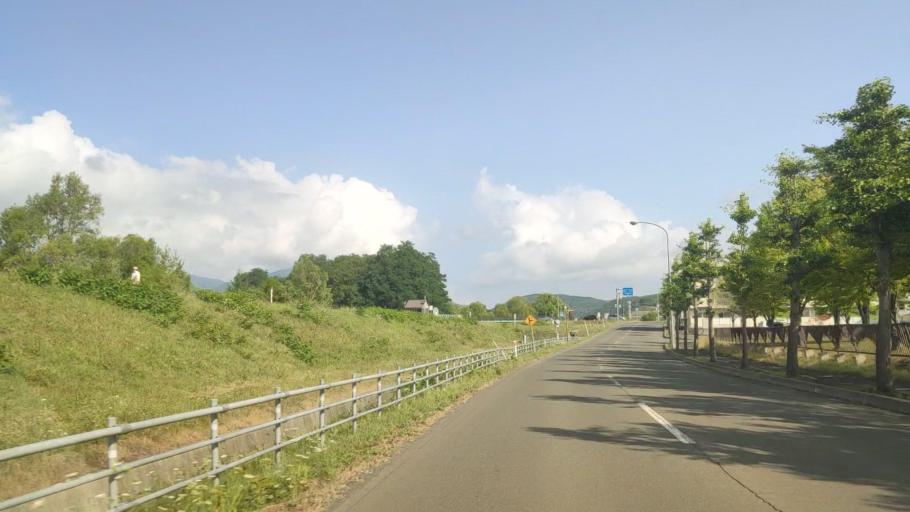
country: JP
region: Hokkaido
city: Shimo-furano
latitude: 43.3436
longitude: 142.3768
